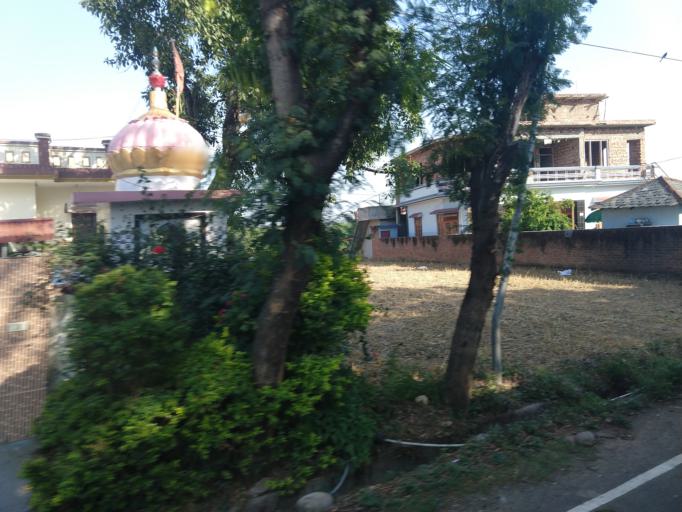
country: IN
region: Himachal Pradesh
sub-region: Chamba
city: Chowari
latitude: 32.3558
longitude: 75.9195
